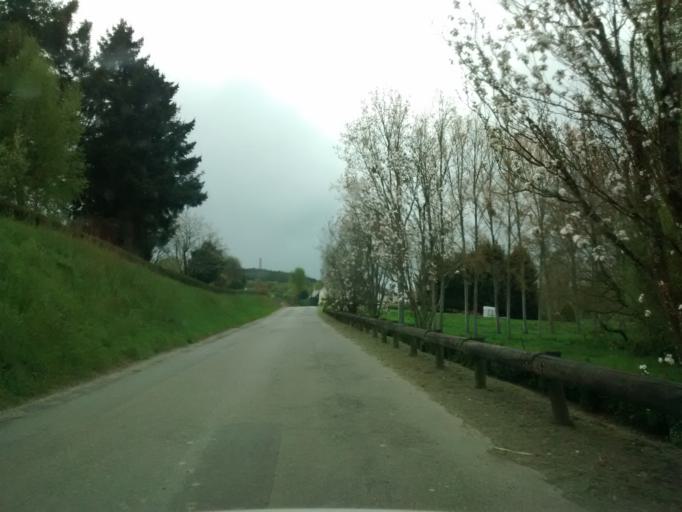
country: FR
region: Brittany
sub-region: Departement du Morbihan
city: Ruffiac
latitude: 47.7926
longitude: -2.3176
